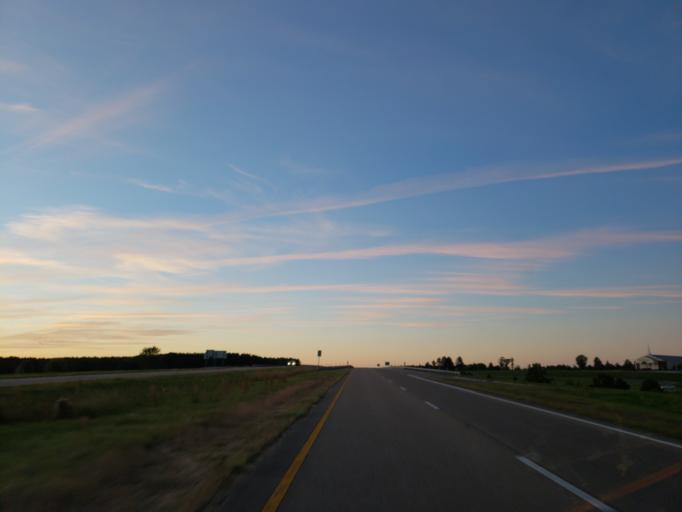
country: US
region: Mississippi
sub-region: Wayne County
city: Waynesboro
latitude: 31.7061
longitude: -88.6249
